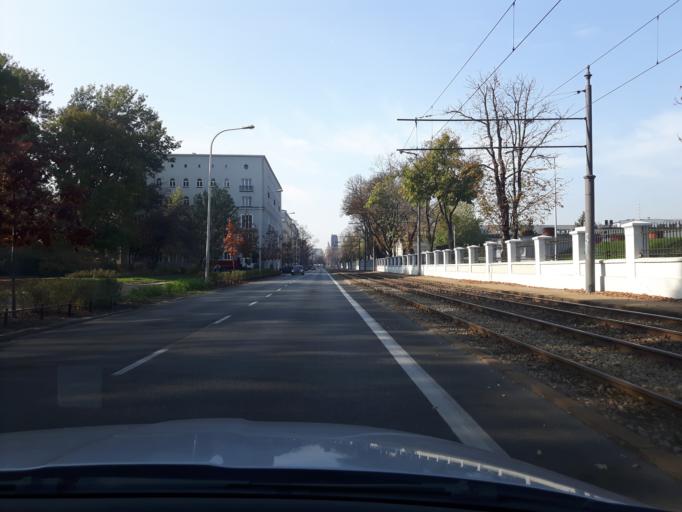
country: PL
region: Masovian Voivodeship
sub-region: Warszawa
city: Ochota
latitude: 52.2190
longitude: 20.9952
